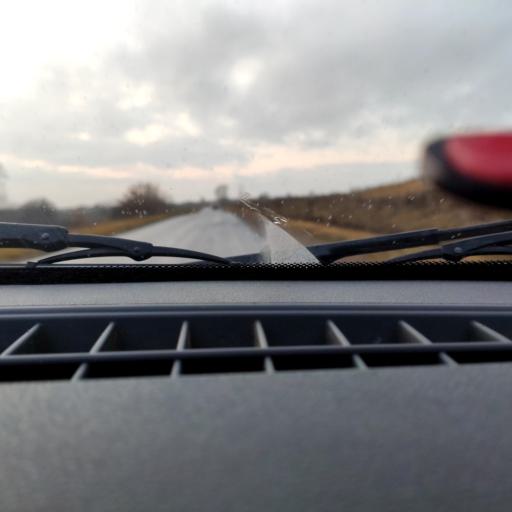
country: RU
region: Bashkortostan
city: Avdon
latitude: 54.5107
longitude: 55.8529
